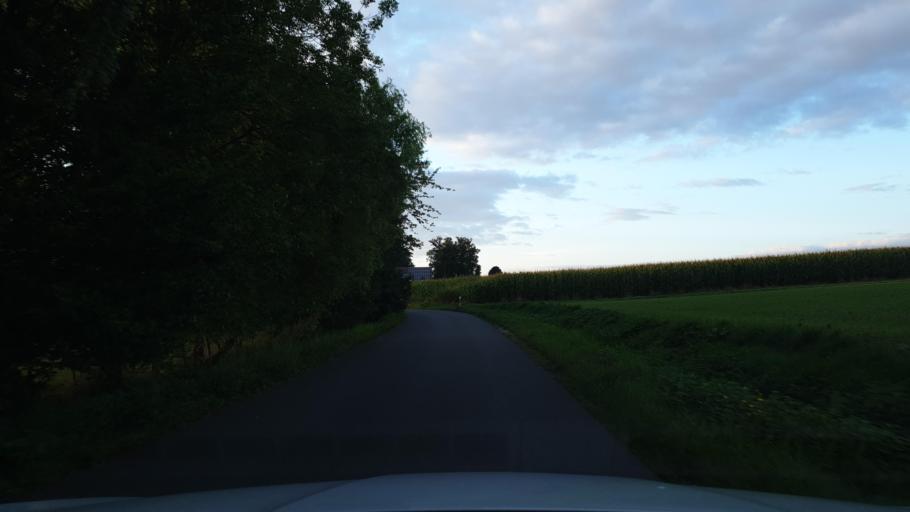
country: DE
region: North Rhine-Westphalia
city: Bad Oeynhausen
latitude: 52.2247
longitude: 8.7525
